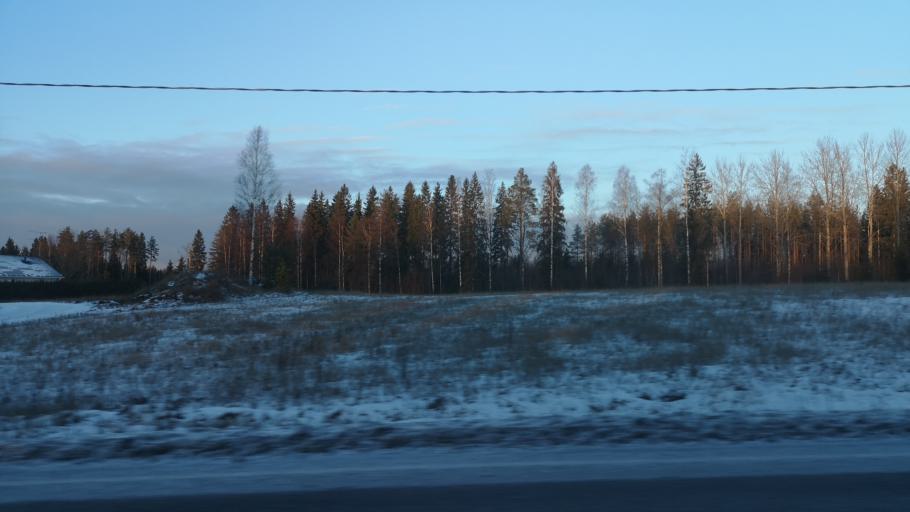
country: FI
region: Southern Savonia
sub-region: Savonlinna
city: Rantasalmi
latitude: 61.9542
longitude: 28.4215
